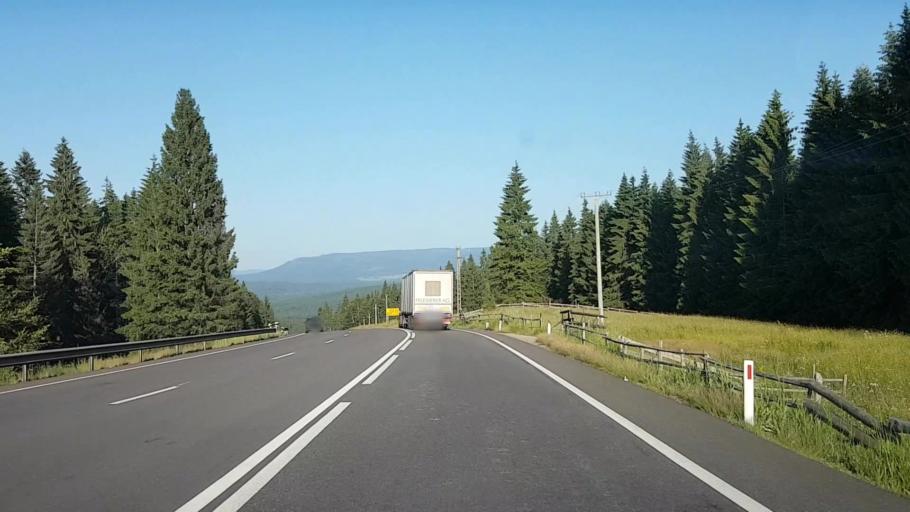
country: RO
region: Suceava
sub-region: Comuna Poiana Stampei
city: Poiana Stampei
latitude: 47.2846
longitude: 25.0432
